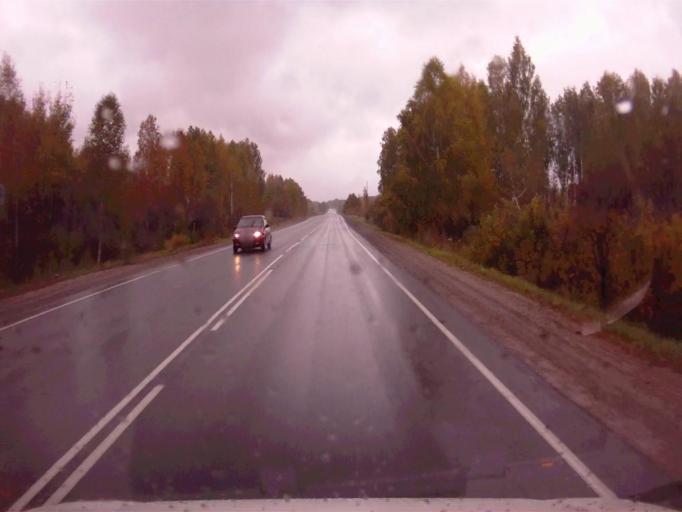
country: RU
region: Chelyabinsk
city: Argayash
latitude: 55.4800
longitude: 60.7572
